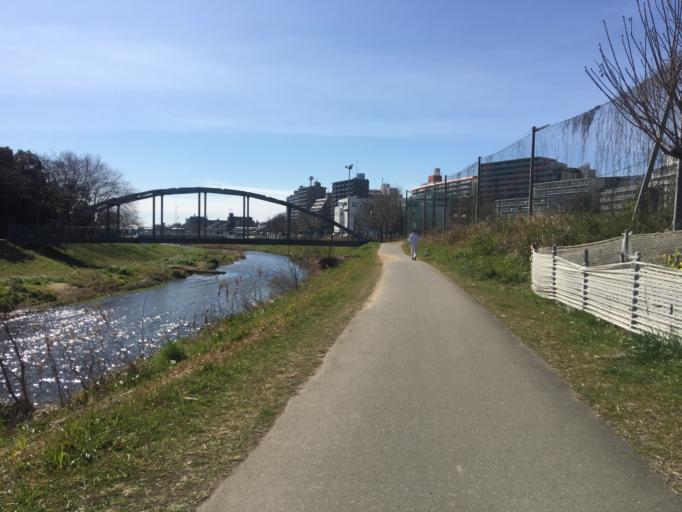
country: JP
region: Saitama
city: Asaka
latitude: 35.8081
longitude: 139.5855
